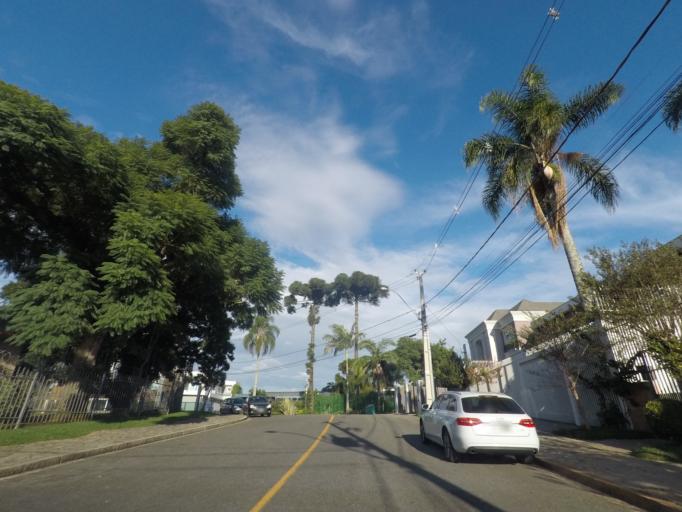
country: BR
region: Parana
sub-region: Curitiba
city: Curitiba
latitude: -25.4530
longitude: -49.3078
